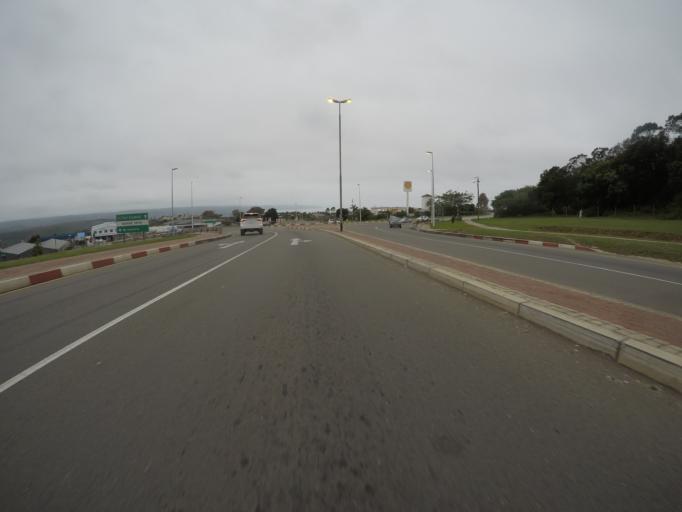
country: ZA
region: Western Cape
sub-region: Eden District Municipality
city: Plettenberg Bay
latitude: -34.0503
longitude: 23.3561
